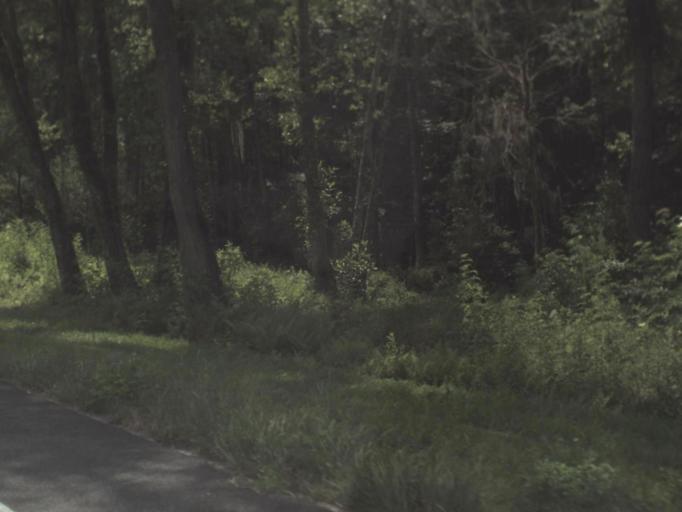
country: US
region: Florida
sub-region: Hamilton County
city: Jasper
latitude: 30.5242
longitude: -82.9887
